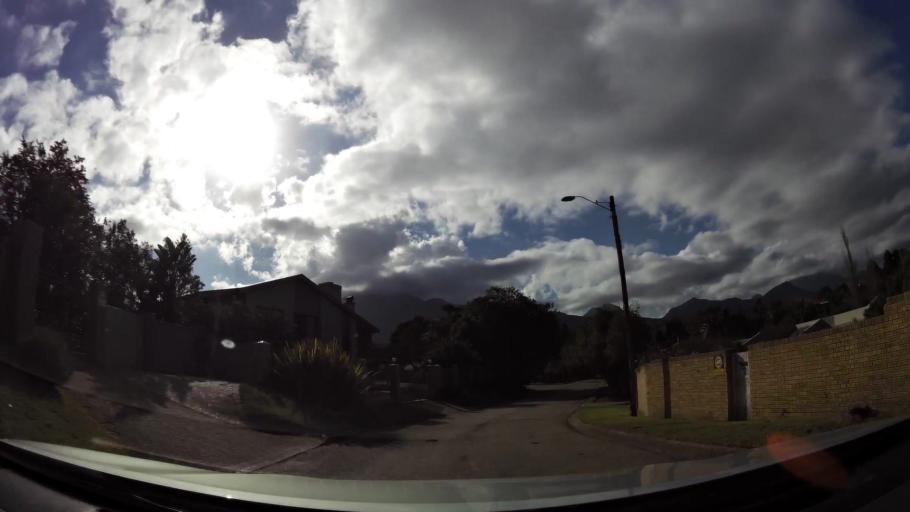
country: ZA
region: Western Cape
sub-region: Eden District Municipality
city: George
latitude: -33.9562
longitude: 22.4791
